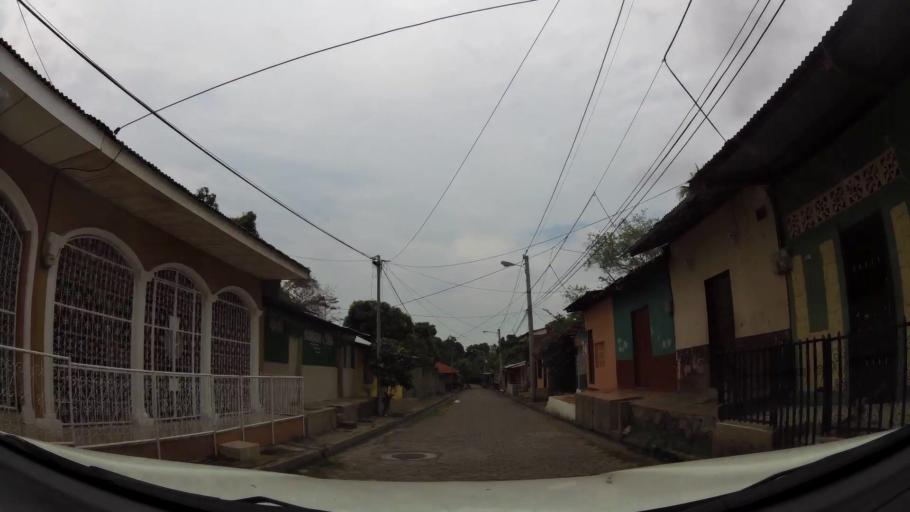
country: NI
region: Granada
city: Granada
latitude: 11.9228
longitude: -85.9615
